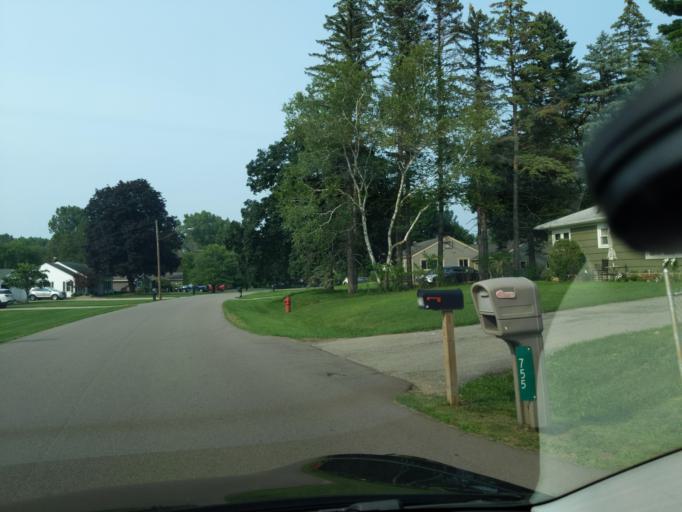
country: US
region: Michigan
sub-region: Jackson County
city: Jackson
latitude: 42.2410
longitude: -84.4466
